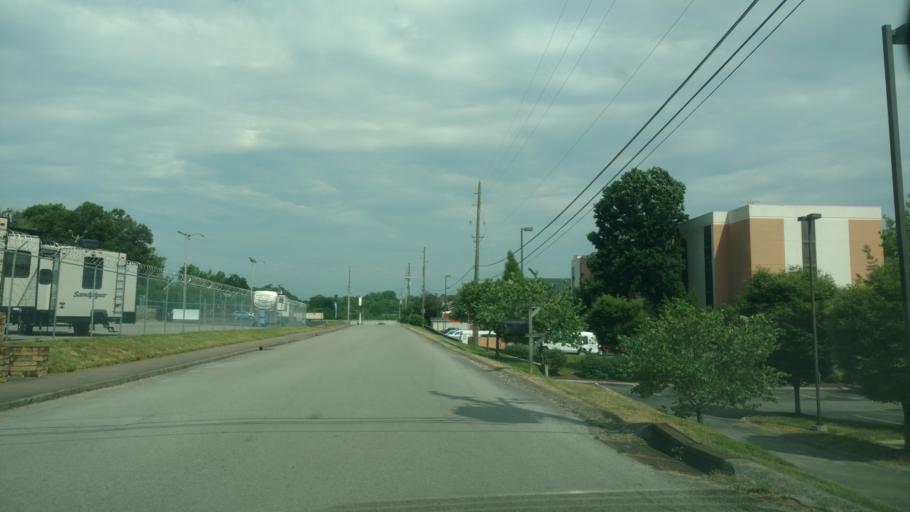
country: US
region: Tennessee
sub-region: Davidson County
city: Lakewood
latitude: 36.2214
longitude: -86.6973
